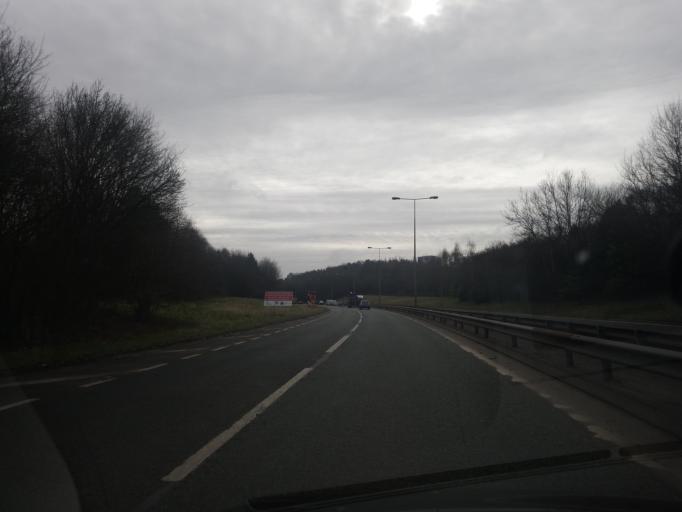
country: GB
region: England
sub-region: Telford and Wrekin
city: Oakengates
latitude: 52.6864
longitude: -2.4465
